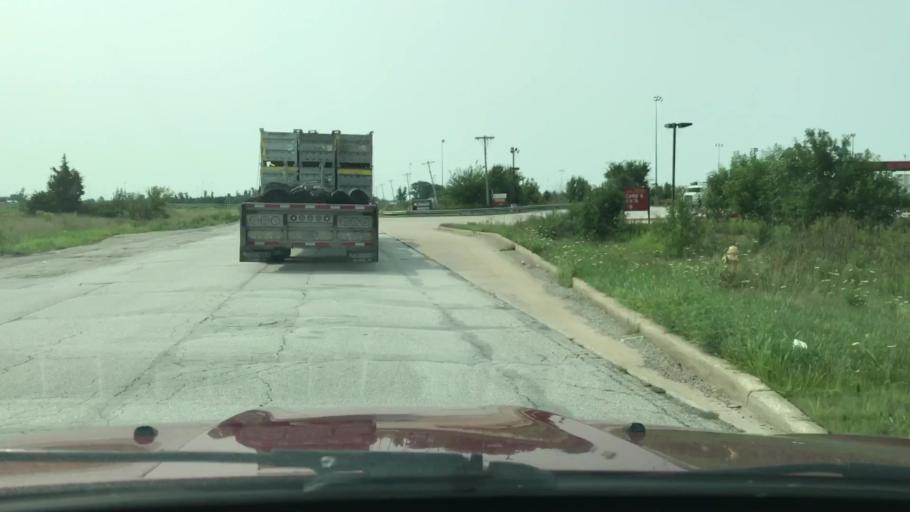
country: US
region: Ohio
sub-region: Wood County
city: Millbury
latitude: 41.5360
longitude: -83.4590
